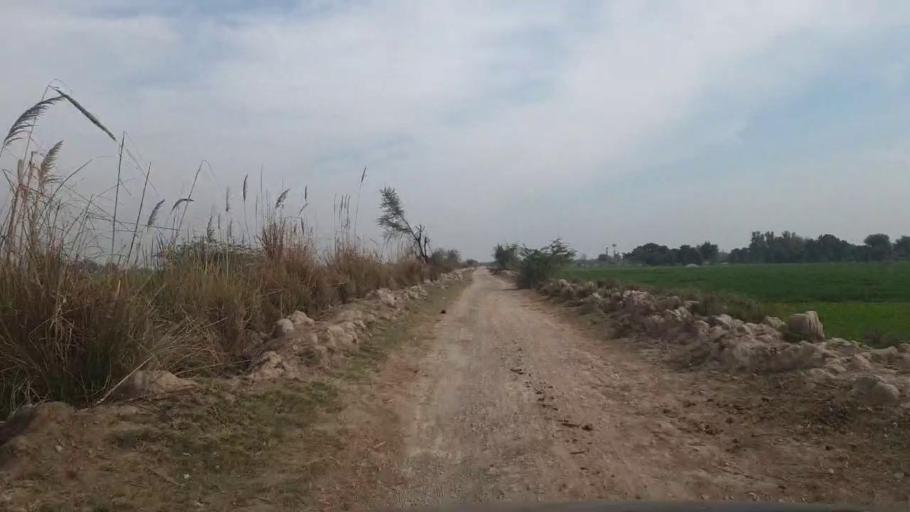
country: PK
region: Sindh
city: Nawabshah
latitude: 26.0757
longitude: 68.4545
